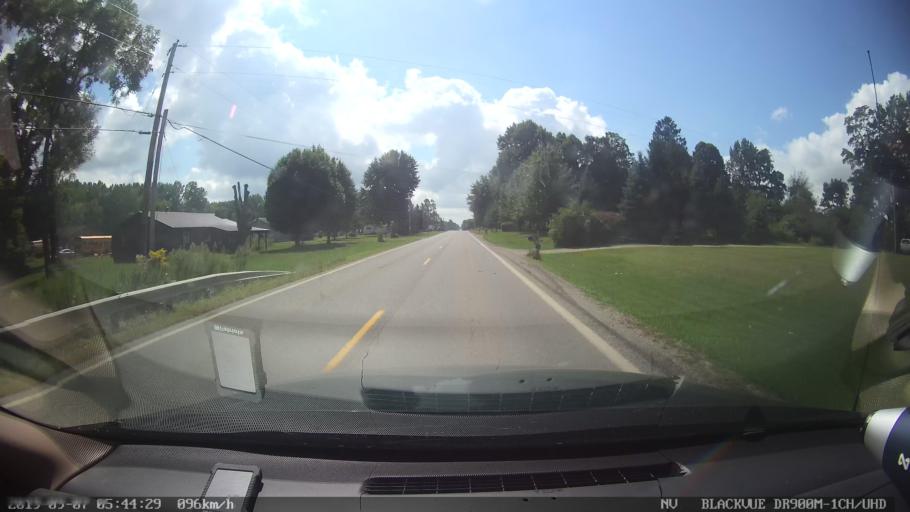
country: US
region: Ohio
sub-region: Crawford County
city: Galion
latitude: 40.6736
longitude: -82.7657
